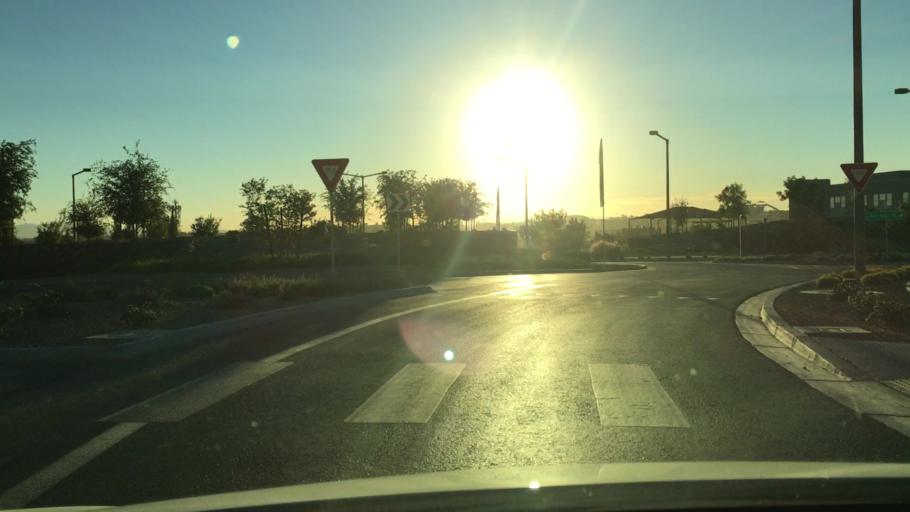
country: US
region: Nevada
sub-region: Clark County
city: Summerlin South
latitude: 36.0627
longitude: -115.3102
